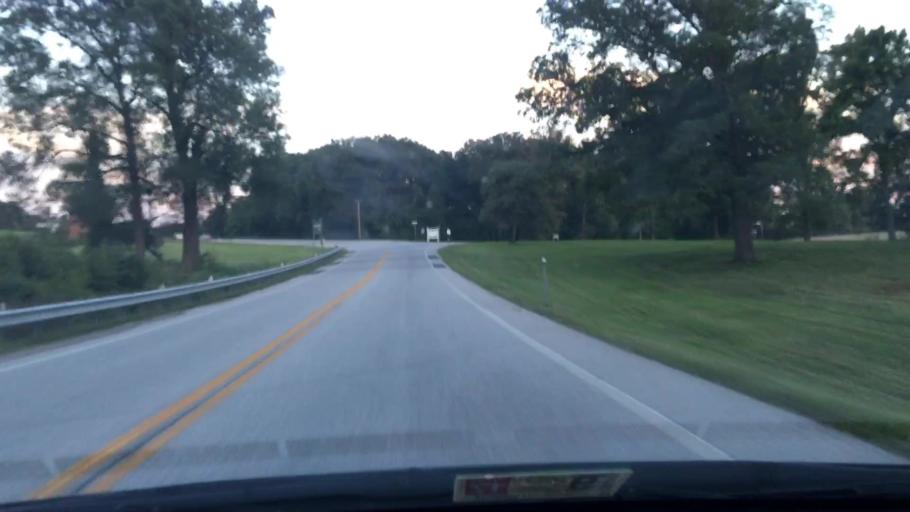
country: US
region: Maryland
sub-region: Prince George's County
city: Greenbelt
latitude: 39.0327
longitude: -76.8780
